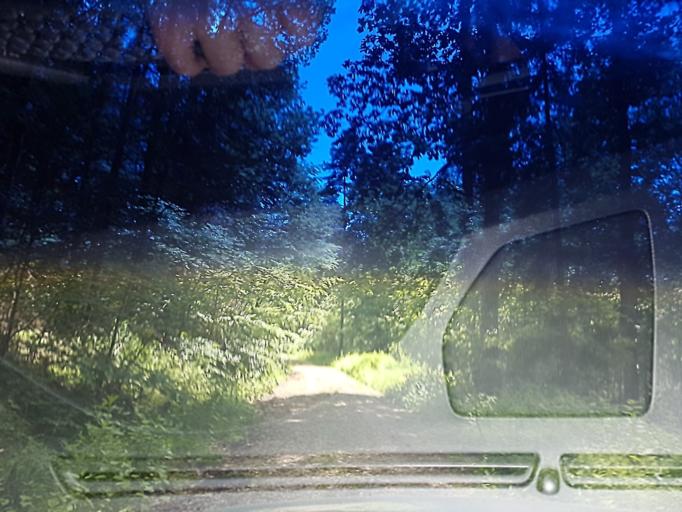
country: DE
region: Bavaria
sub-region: Upper Franconia
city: Litzendorf
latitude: 49.9405
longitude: 11.0239
